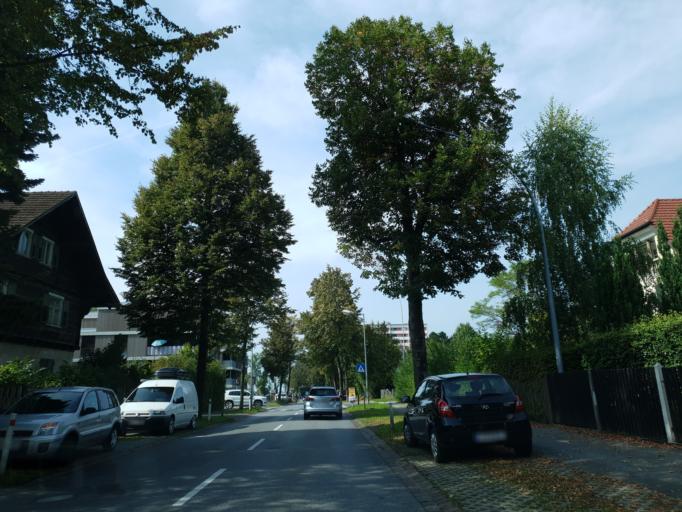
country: AT
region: Vorarlberg
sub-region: Politischer Bezirk Bregenz
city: Bregenz
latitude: 47.4958
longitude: 9.7371
